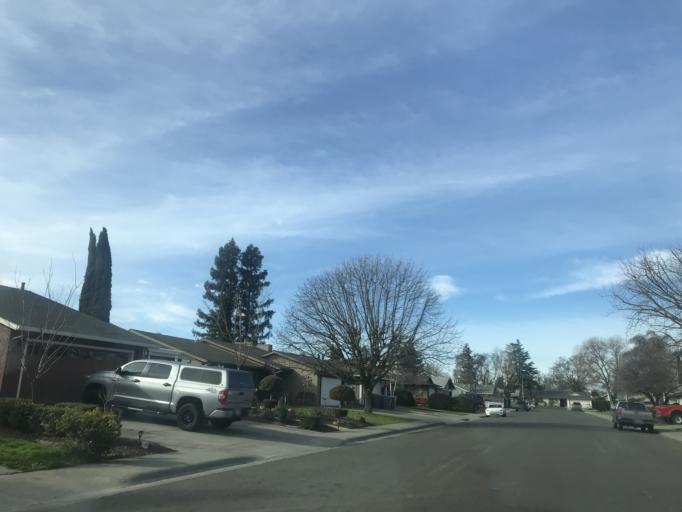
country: US
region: California
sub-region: Yolo County
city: Woodland
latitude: 38.6675
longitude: -121.7532
